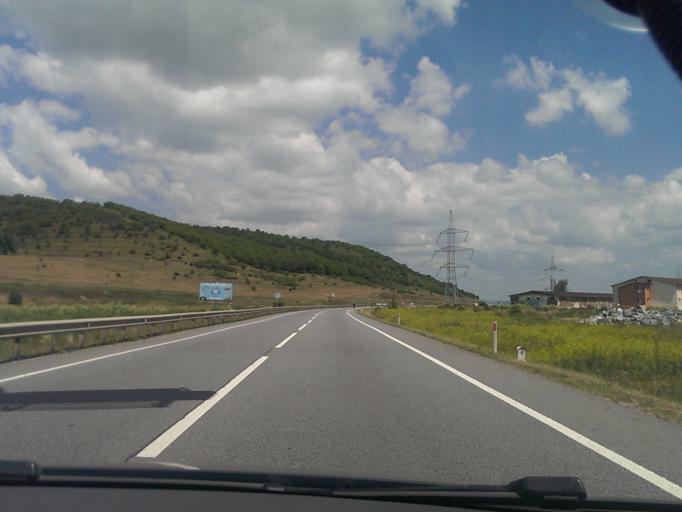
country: RO
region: Cluj
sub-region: Comuna Apahida
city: Apahida
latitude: 46.8121
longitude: 23.7364
